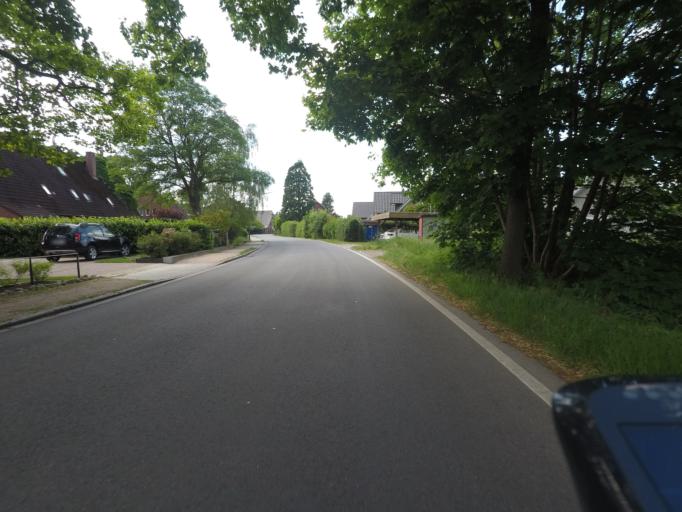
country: DE
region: Lower Saxony
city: Drage
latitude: 53.4378
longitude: 10.2357
